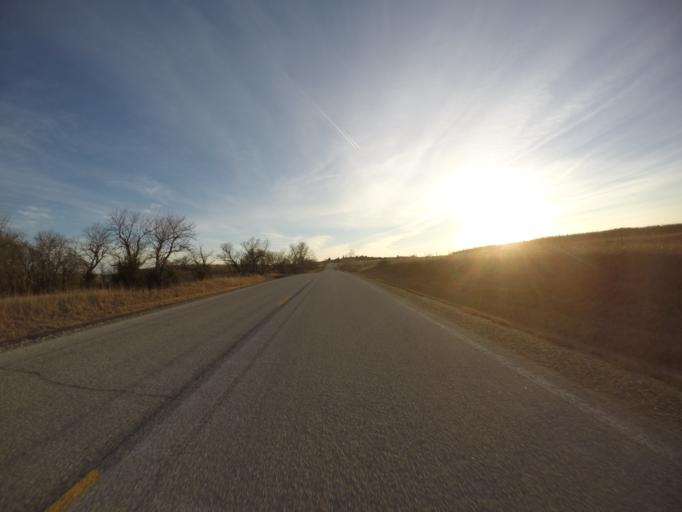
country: US
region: Kansas
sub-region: Riley County
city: Ogden
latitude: 39.3010
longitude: -96.7510
